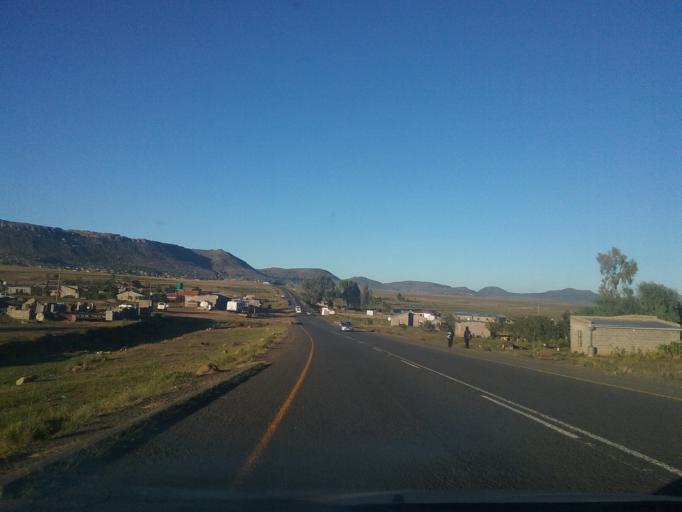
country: LS
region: Mohale's Hoek District
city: Mohale's Hoek
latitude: -30.1538
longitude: 27.4406
